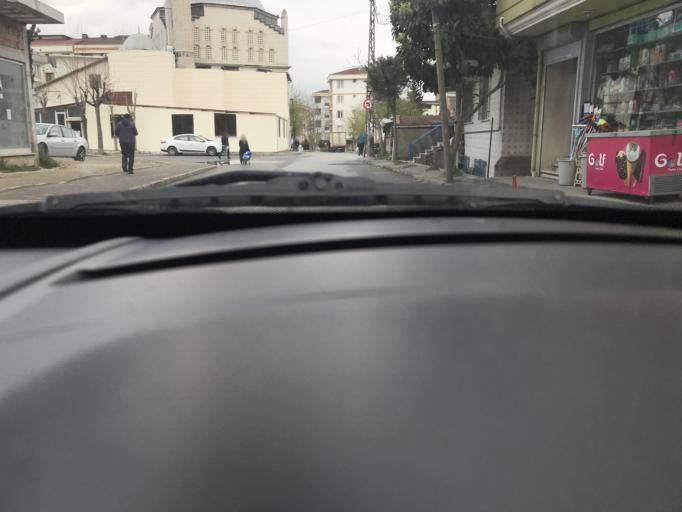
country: TR
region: Istanbul
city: Yakuplu
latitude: 41.0031
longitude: 28.6952
